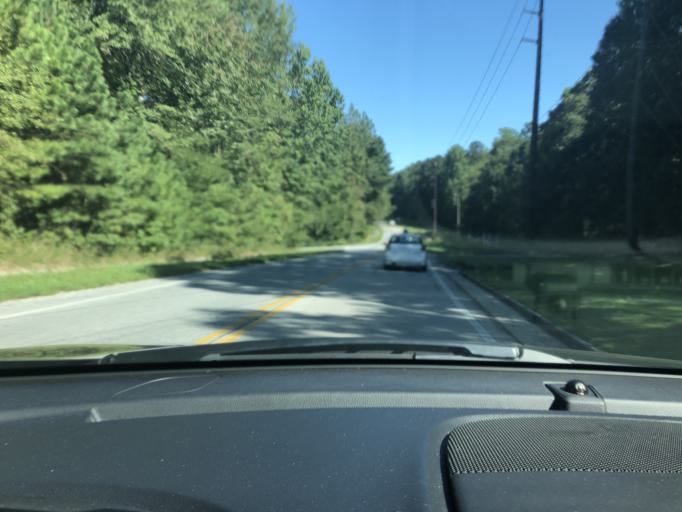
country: US
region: Georgia
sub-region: Gwinnett County
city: Grayson
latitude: 33.9204
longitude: -83.9436
